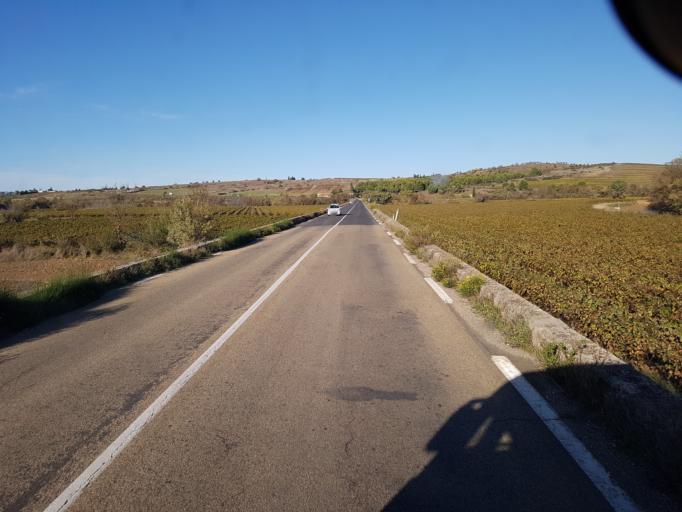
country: FR
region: Languedoc-Roussillon
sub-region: Departement de l'Aude
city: Coursan
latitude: 43.2616
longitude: 3.0780
